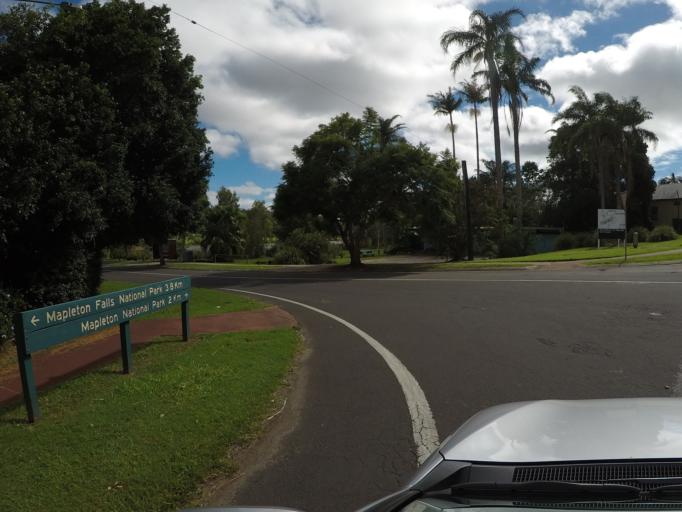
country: AU
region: Queensland
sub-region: Sunshine Coast
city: Nambour
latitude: -26.6246
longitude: 152.8651
